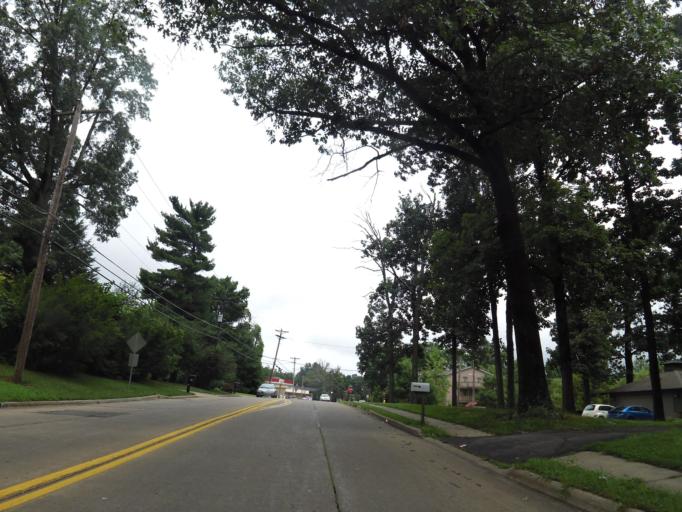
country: US
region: Missouri
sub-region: Cape Girardeau County
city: Cape Girardeau
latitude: 37.3374
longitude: -89.5526
